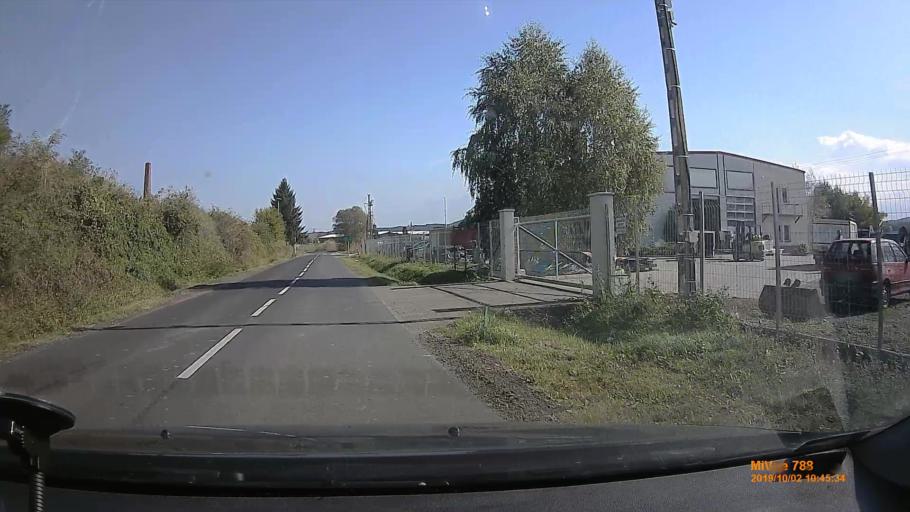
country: HU
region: Nograd
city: Batonyterenye
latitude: 47.9934
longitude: 19.8142
